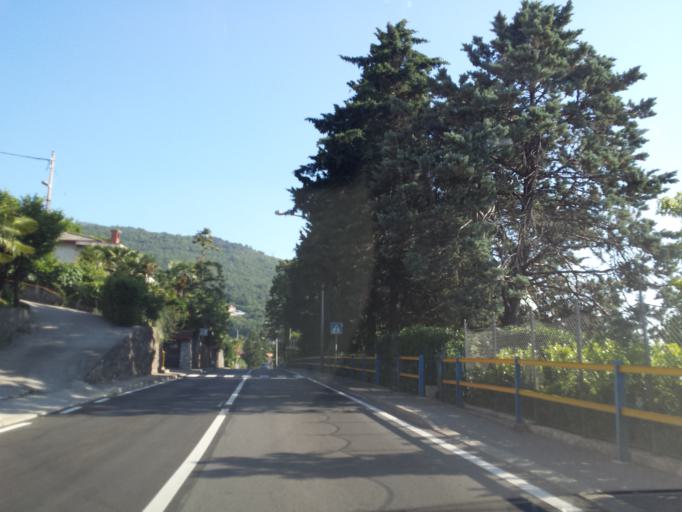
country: HR
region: Primorsko-Goranska
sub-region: Grad Opatija
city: Opatija
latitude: 45.3304
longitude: 14.2998
